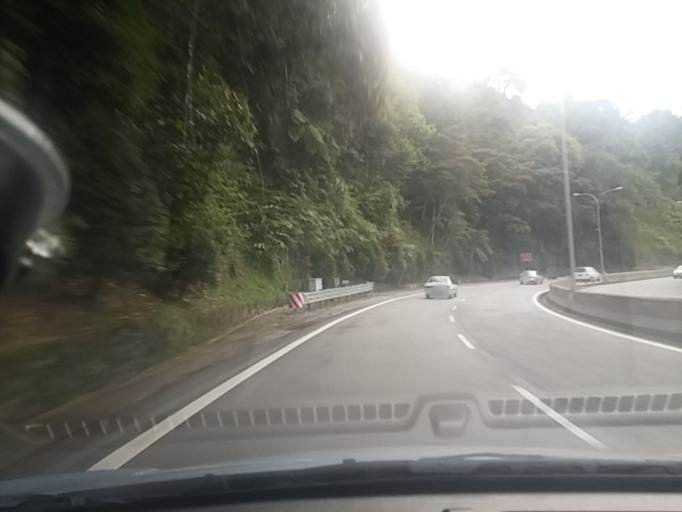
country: MY
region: Pahang
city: Kampung Bukit Tinggi, Bentong
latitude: 3.3769
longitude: 101.7740
